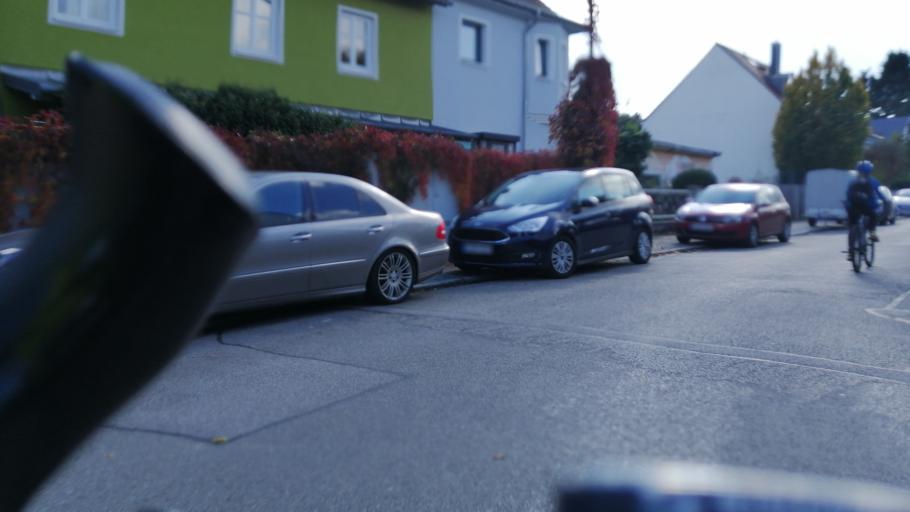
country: DE
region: Bavaria
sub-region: Upper Bavaria
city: Pasing
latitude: 48.1322
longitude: 11.4939
